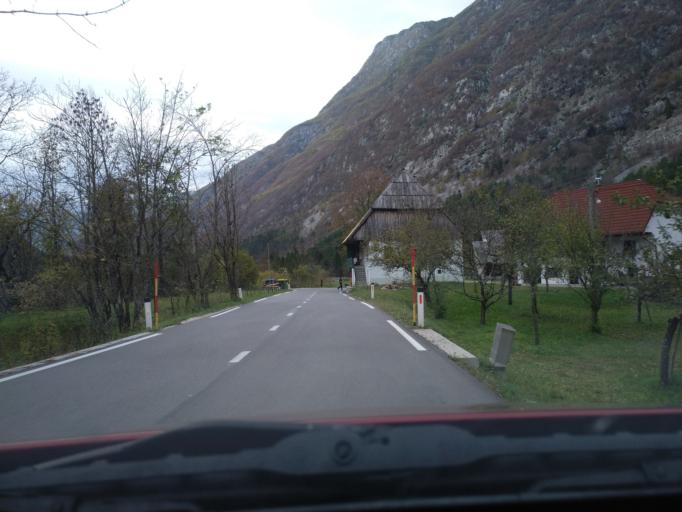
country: SI
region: Bovec
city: Bovec
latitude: 46.3350
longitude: 13.6380
